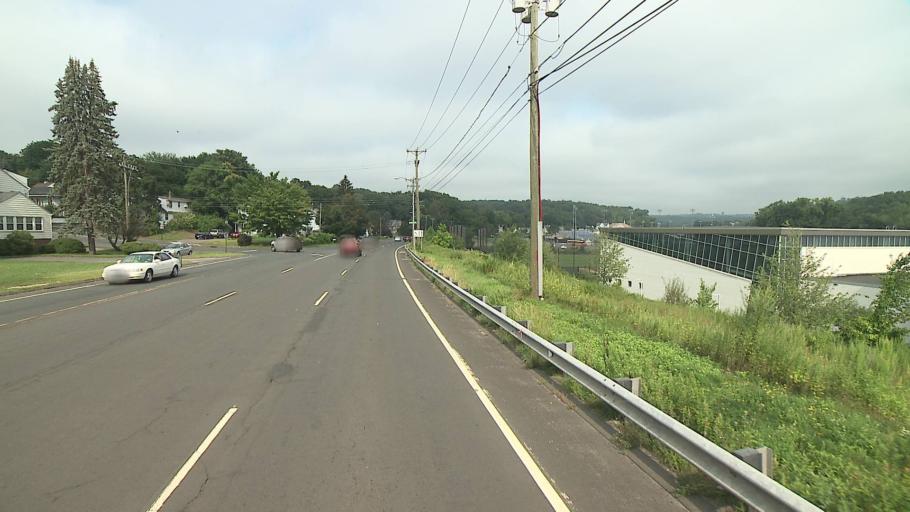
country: US
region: Connecticut
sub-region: New Haven County
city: Waterbury
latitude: 41.5744
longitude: -73.0669
